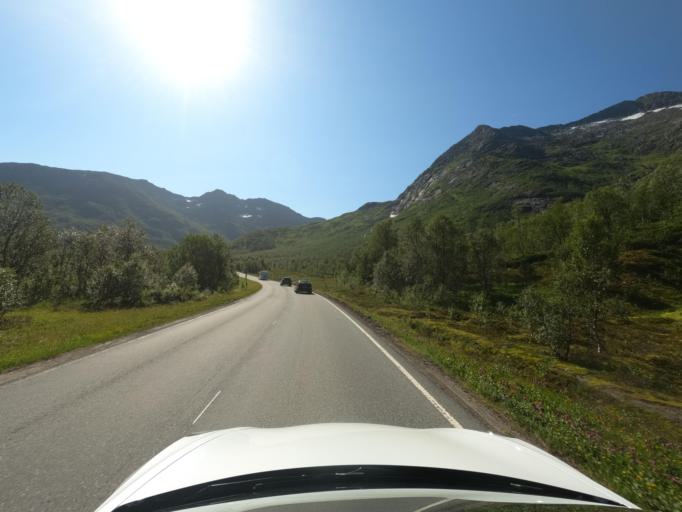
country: NO
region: Nordland
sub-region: Lodingen
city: Lodingen
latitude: 68.5337
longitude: 15.7238
